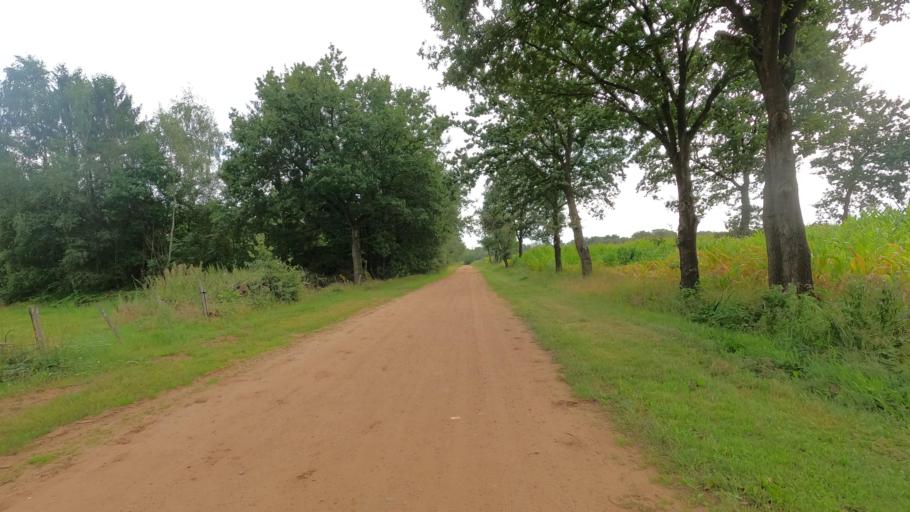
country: BE
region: Flanders
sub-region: Provincie Antwerpen
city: Lille
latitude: 51.2408
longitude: 4.7886
